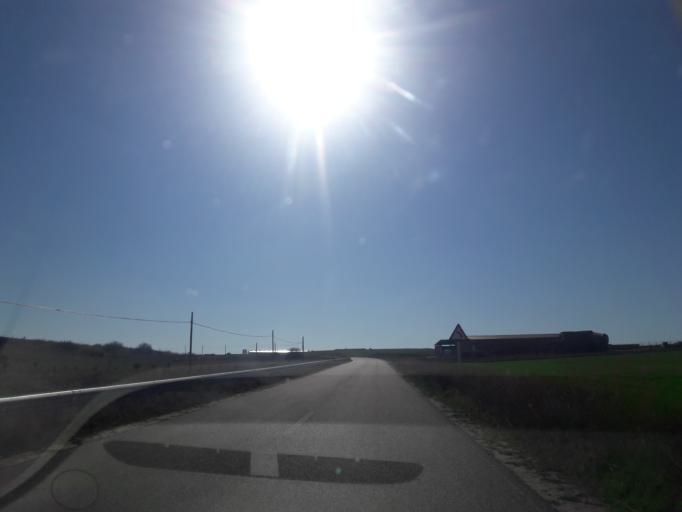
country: ES
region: Castille and Leon
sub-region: Provincia de Salamanca
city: Tordillos
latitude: 40.8522
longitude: -5.3417
